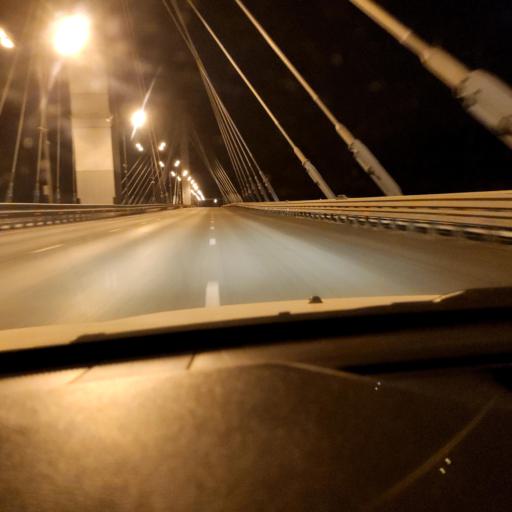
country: RU
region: Samara
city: Smyshlyayevka
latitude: 53.1806
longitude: 50.3063
